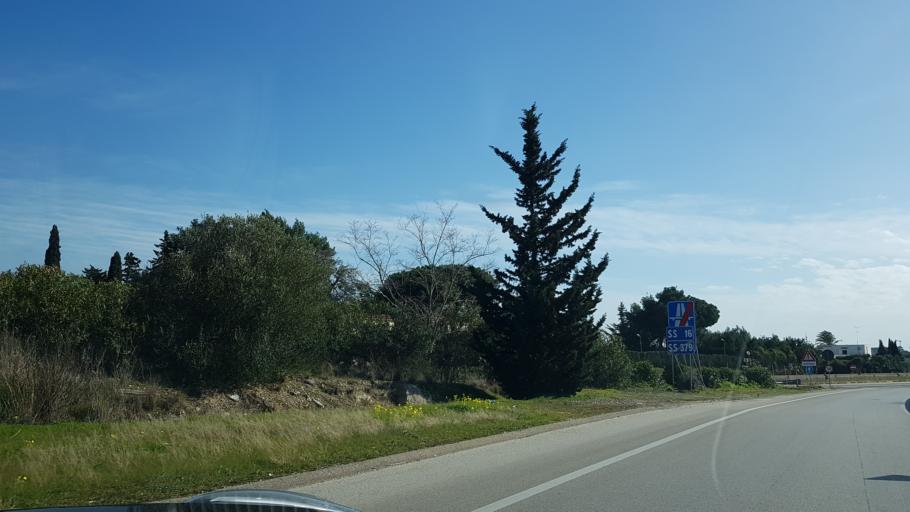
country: IT
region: Apulia
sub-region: Provincia di Brindisi
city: Brindisi
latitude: 40.6421
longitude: 17.9140
